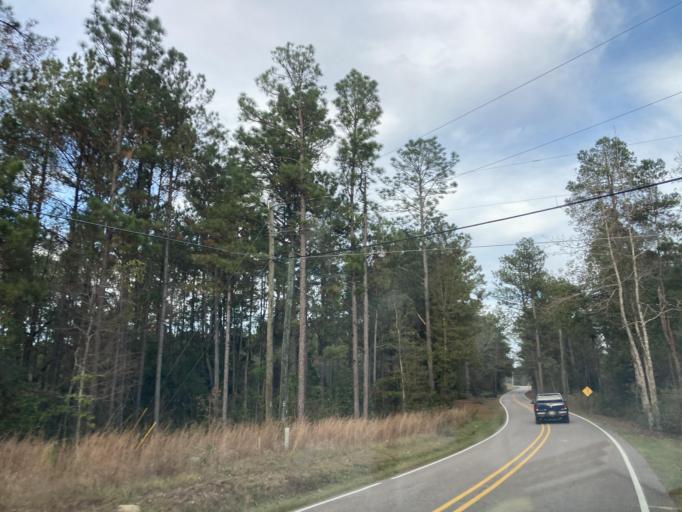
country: US
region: Mississippi
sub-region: Lamar County
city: Purvis
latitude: 31.1825
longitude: -89.3545
